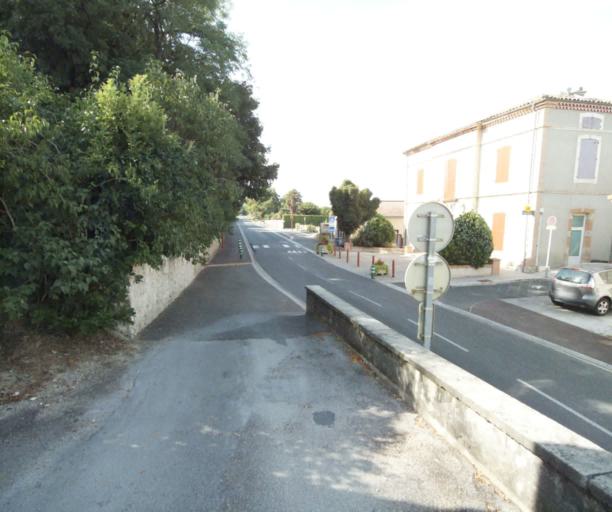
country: FR
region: Midi-Pyrenees
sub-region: Departement du Tarn
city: Soual
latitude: 43.5286
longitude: 2.0645
